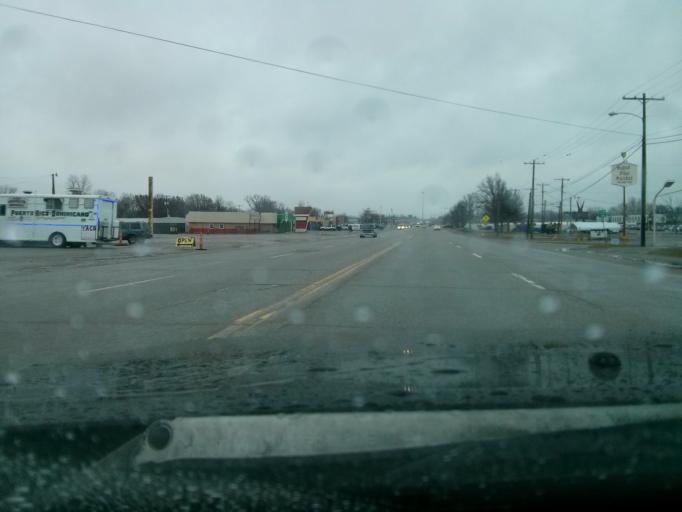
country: US
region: Oklahoma
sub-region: Tulsa County
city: Owasso
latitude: 36.1607
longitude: -95.8757
